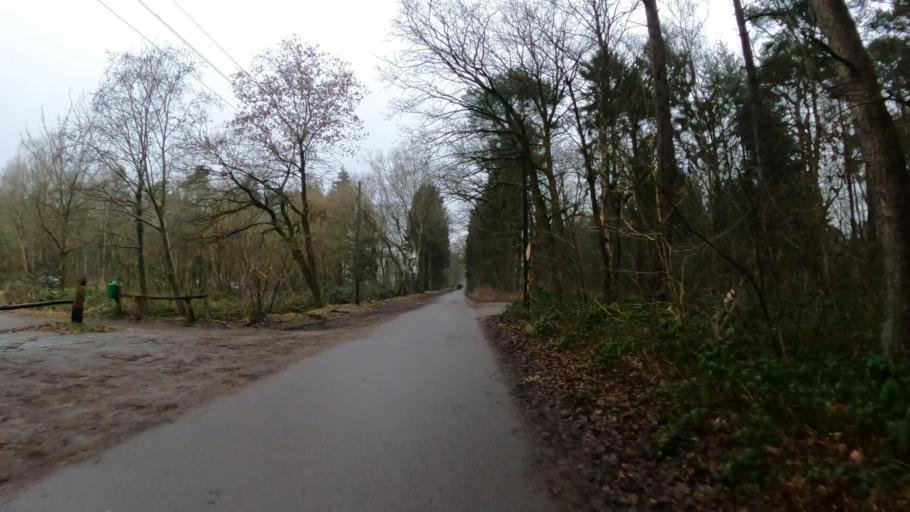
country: DE
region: Schleswig-Holstein
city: Wedel
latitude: 53.5973
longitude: 9.7467
